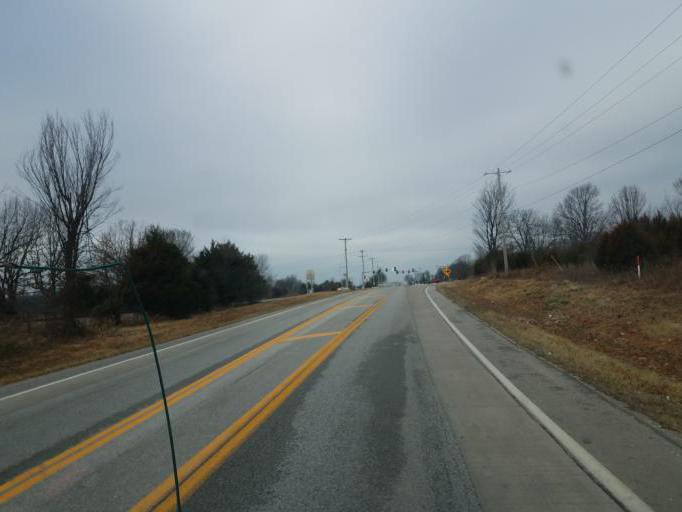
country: US
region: Missouri
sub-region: Greene County
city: Strafford
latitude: 37.2473
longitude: -93.1809
